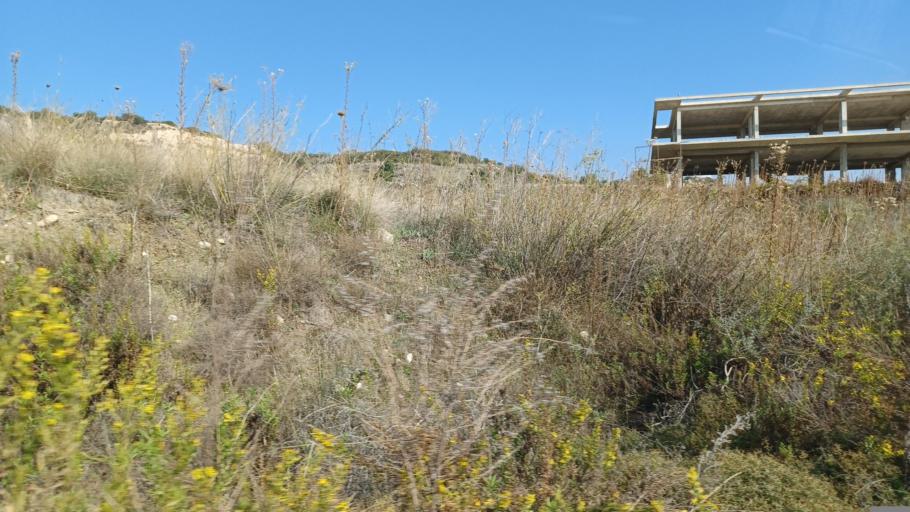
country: CY
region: Pafos
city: Kissonerga
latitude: 34.8457
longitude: 32.3949
